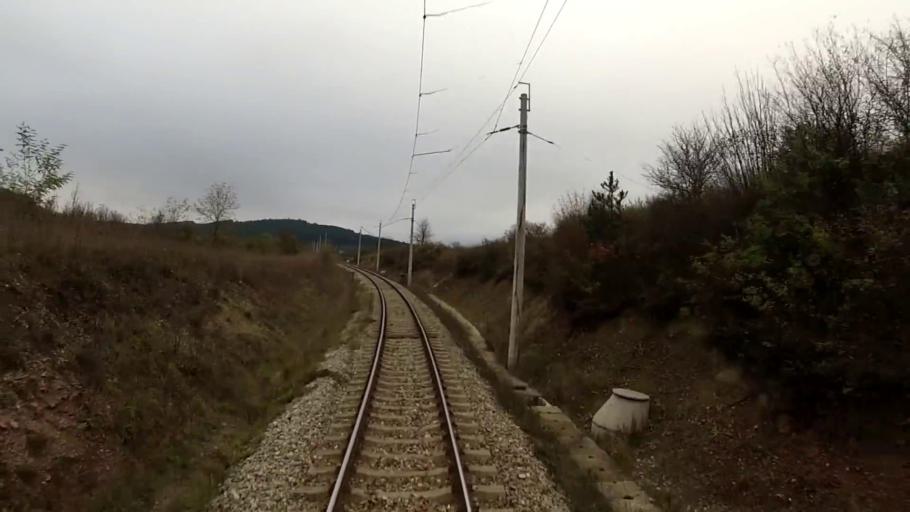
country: BG
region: Sofiya
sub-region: Obshtina Dragoman
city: Dragoman
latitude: 42.9404
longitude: 22.9013
